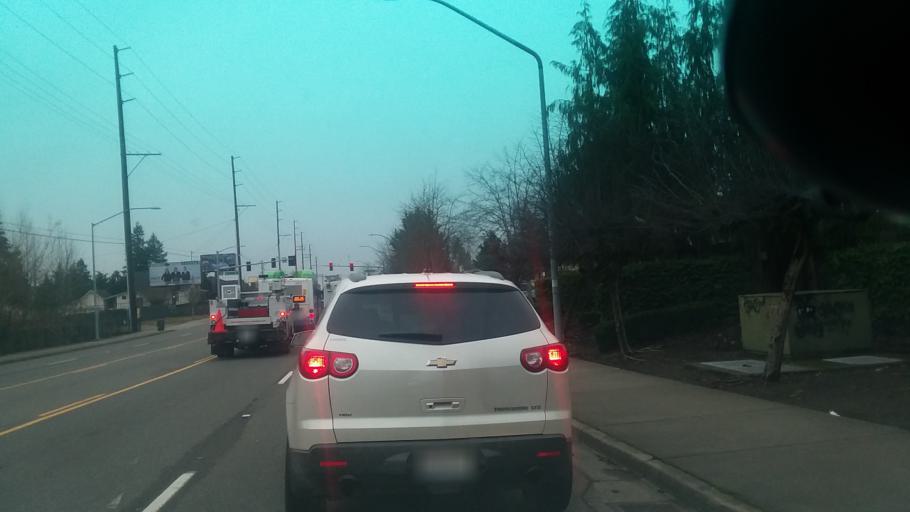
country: US
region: Washington
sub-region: Pierce County
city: South Hill
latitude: 47.1549
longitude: -122.2970
